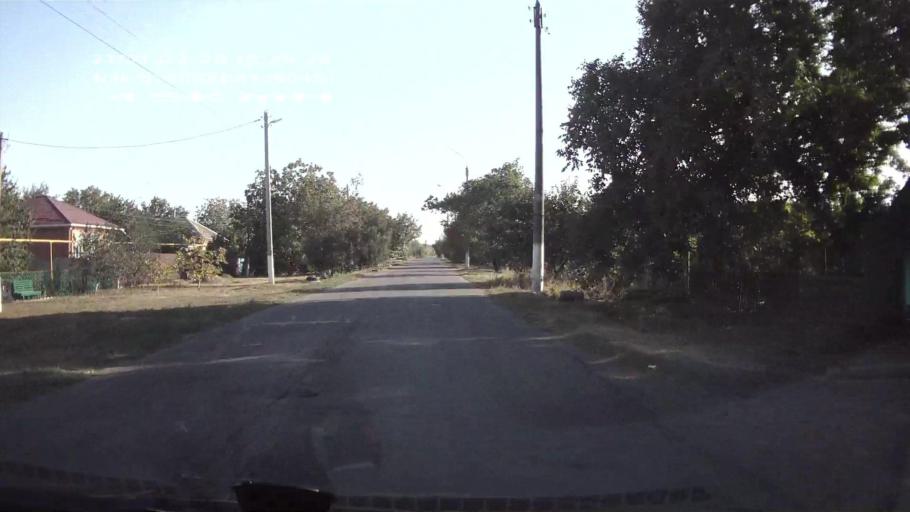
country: RU
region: Rostov
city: Gigant
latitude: 46.5239
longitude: 41.1906
